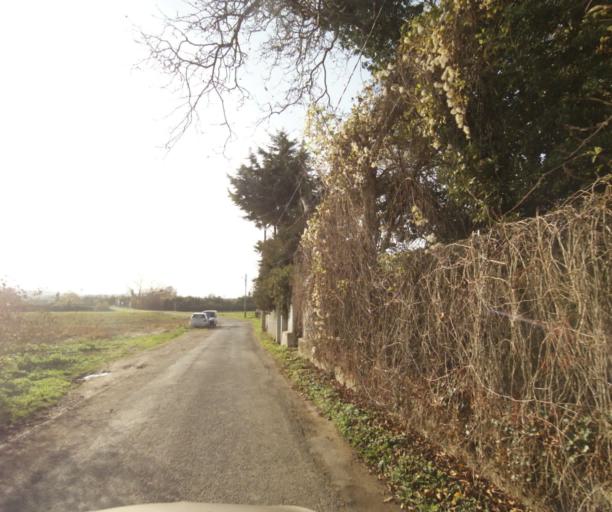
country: FR
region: Ile-de-France
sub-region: Departement des Yvelines
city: Chanteloup-les-Vignes
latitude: 48.9680
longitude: 2.0265
